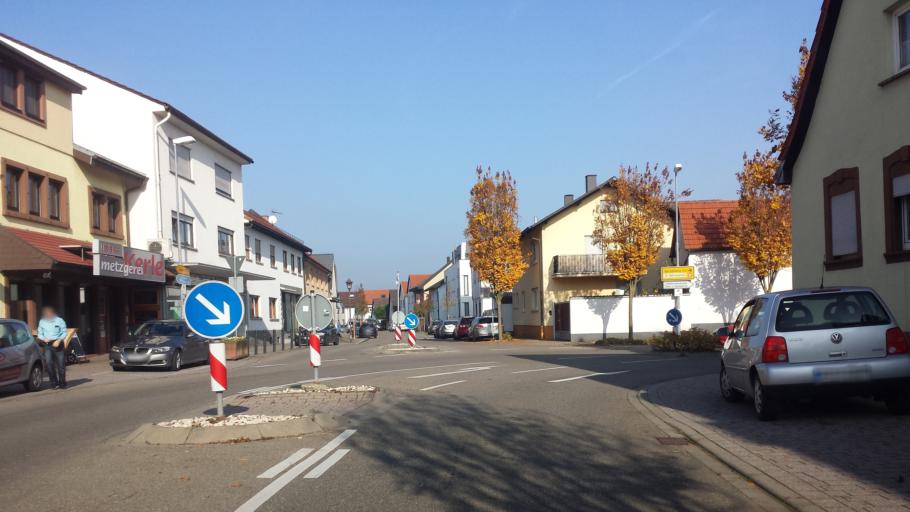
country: DE
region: Baden-Wuerttemberg
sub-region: Karlsruhe Region
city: Kronau
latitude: 49.2208
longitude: 8.6344
